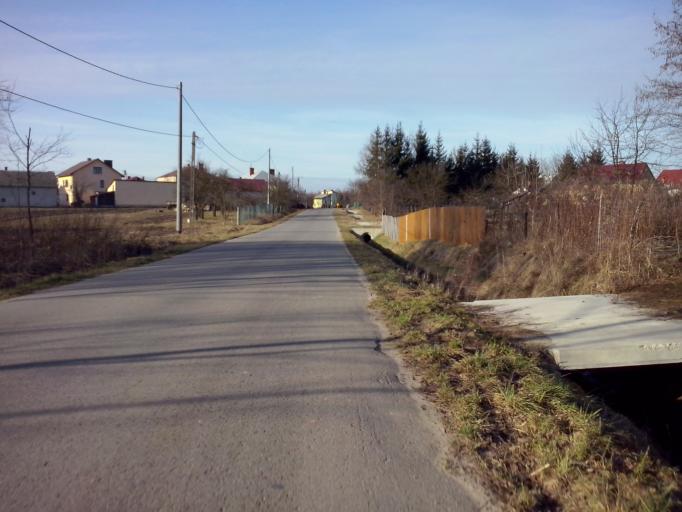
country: PL
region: Subcarpathian Voivodeship
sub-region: Powiat nizanski
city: Krzeszow
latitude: 50.4140
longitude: 22.3503
